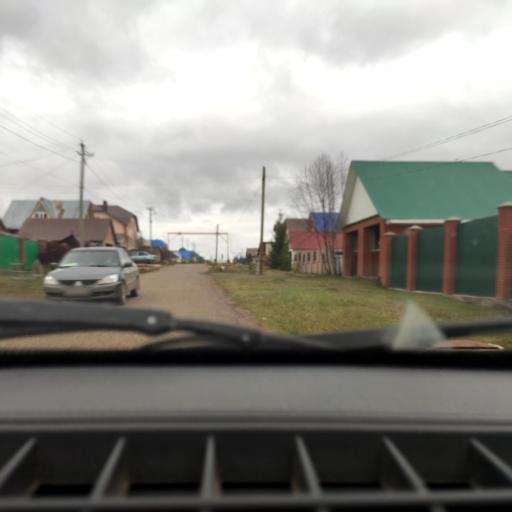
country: RU
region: Bashkortostan
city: Mikhaylovka
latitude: 54.8167
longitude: 55.8902
